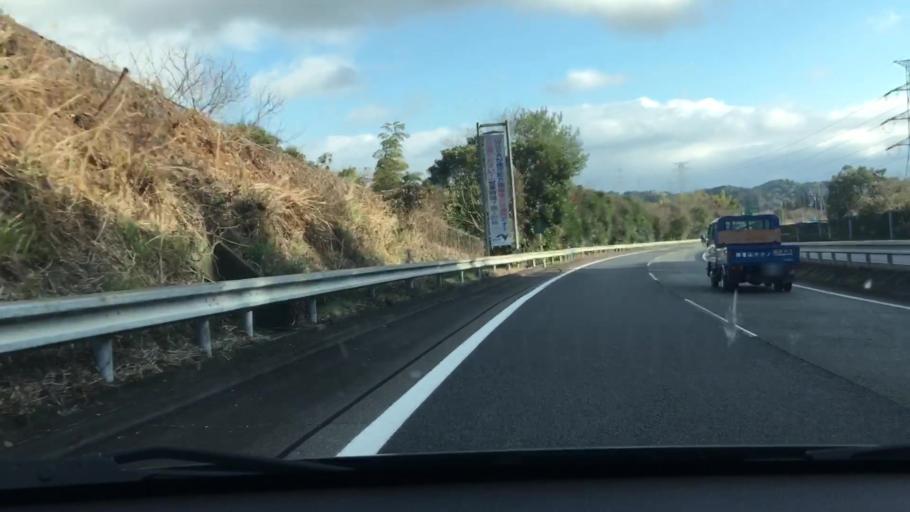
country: JP
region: Kumamoto
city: Hitoyoshi
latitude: 32.2659
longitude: 130.7653
